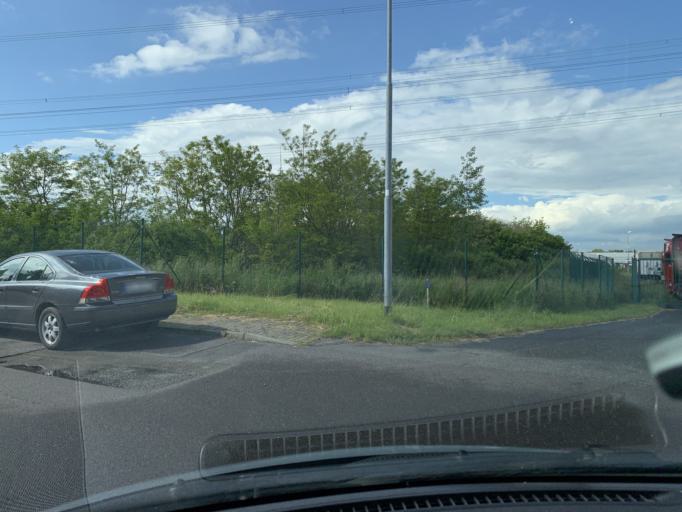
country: DE
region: Brandenburg
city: Nauen
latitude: 52.5951
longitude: 12.8990
